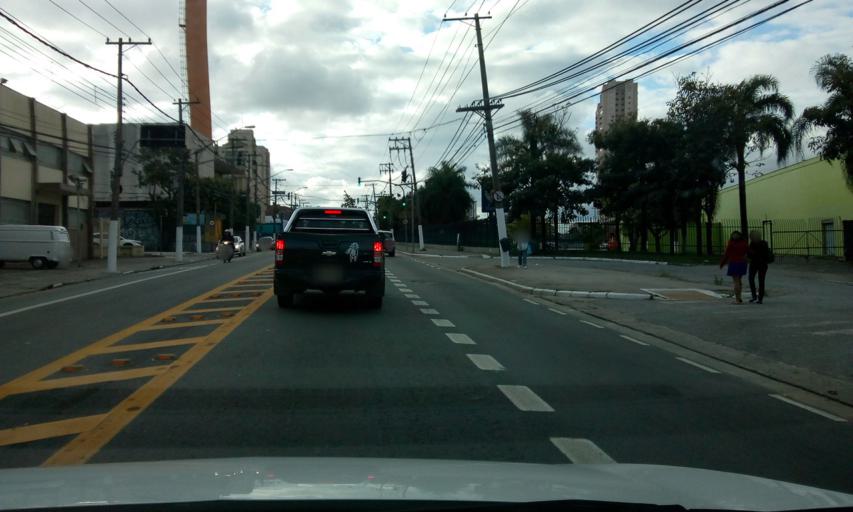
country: BR
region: Sao Paulo
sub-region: Sao Caetano Do Sul
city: Sao Caetano do Sul
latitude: -23.5623
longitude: -46.5164
